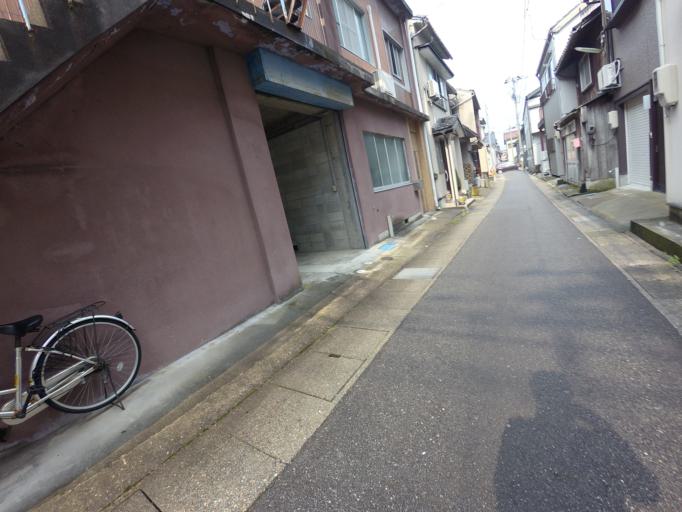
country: JP
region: Ishikawa
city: Nanao
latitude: 37.0482
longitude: 136.9620
